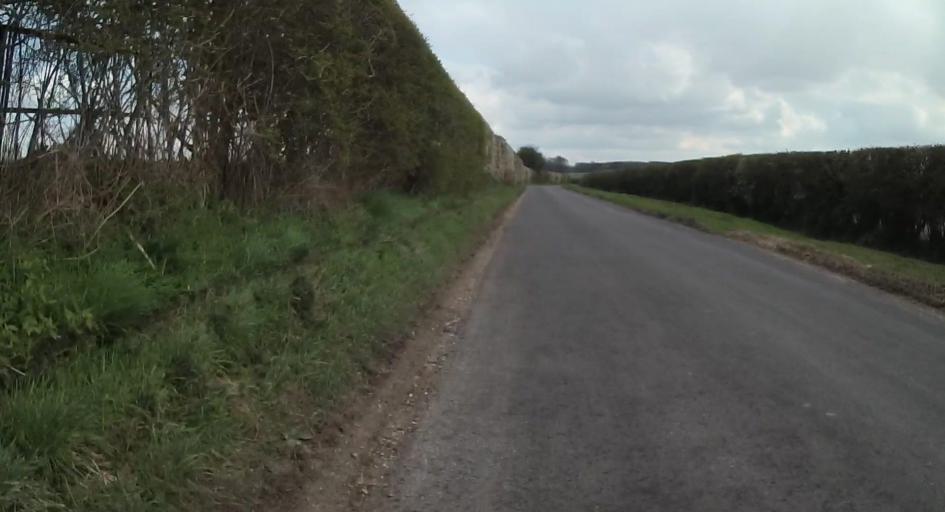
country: GB
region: England
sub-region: Hampshire
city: Basingstoke
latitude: 51.1744
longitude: -1.1246
